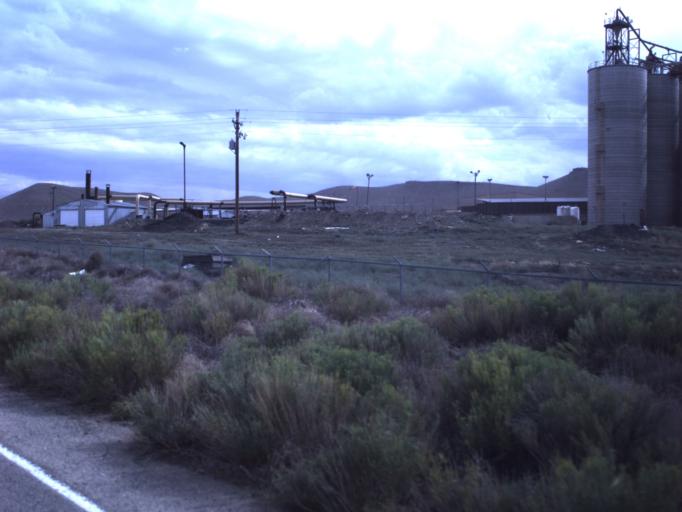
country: US
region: Colorado
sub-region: Rio Blanco County
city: Rangely
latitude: 40.0179
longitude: -109.1725
